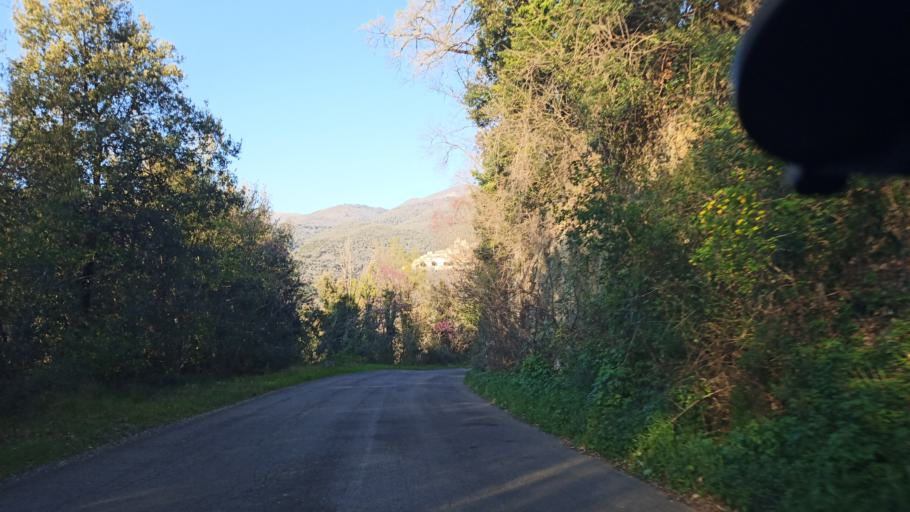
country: IT
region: Latium
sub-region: Provincia di Rieti
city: Roccantica
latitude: 42.3152
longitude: 12.6805
